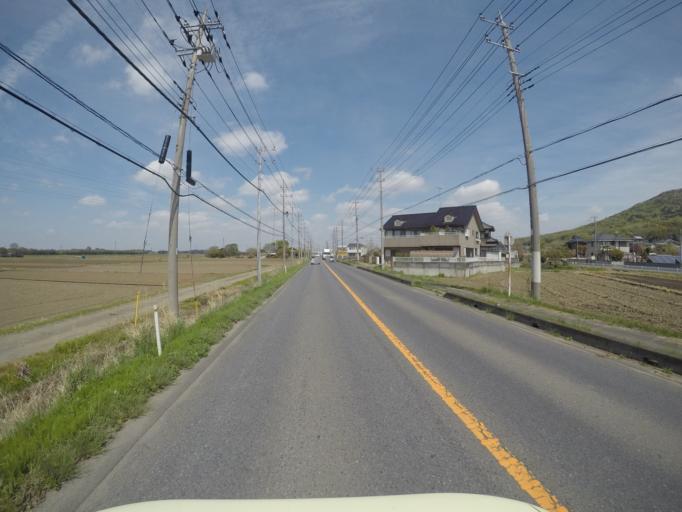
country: JP
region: Ibaraki
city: Tsukuba
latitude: 36.2141
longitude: 140.0687
